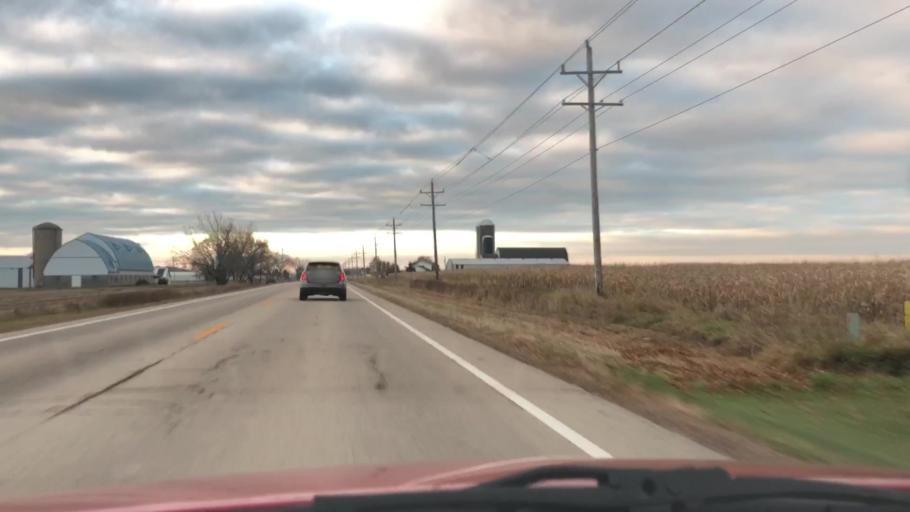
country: US
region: Wisconsin
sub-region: Outagamie County
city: Seymour
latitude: 44.4539
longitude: -88.2913
